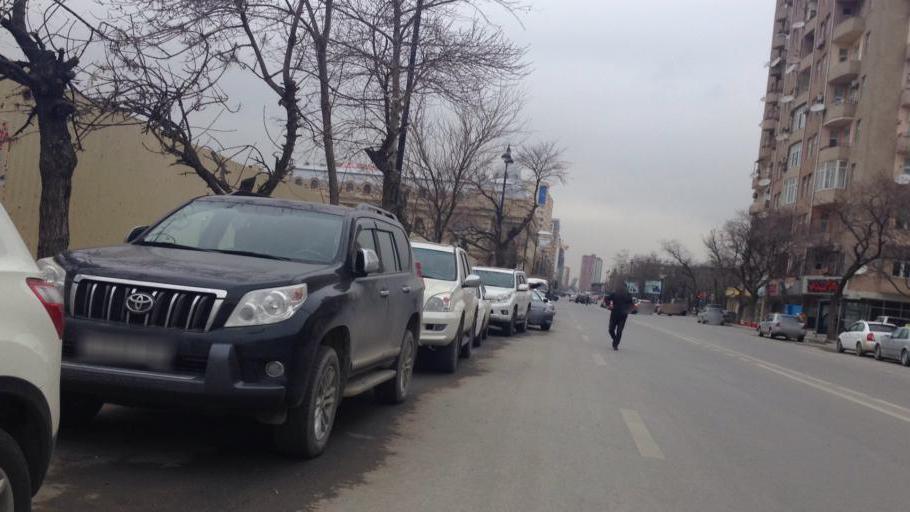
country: AZ
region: Baki
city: Baku
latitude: 40.3896
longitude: 49.8466
